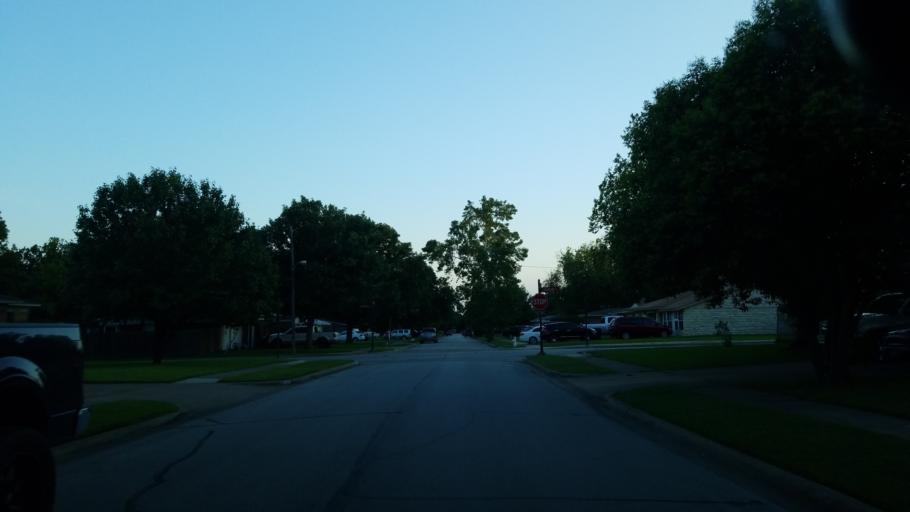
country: US
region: Texas
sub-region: Dallas County
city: Farmers Branch
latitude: 32.9347
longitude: -96.8832
